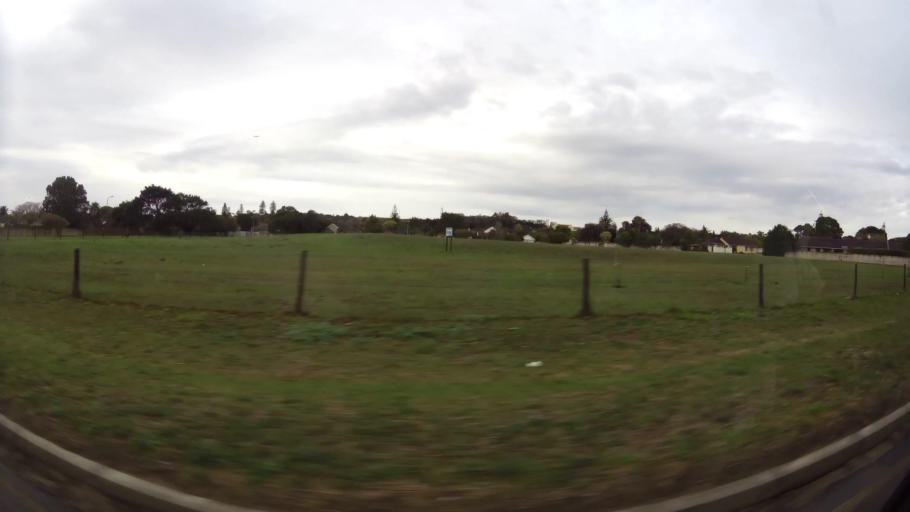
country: ZA
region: Eastern Cape
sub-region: Nelson Mandela Bay Metropolitan Municipality
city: Port Elizabeth
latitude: -33.9923
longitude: 25.5476
